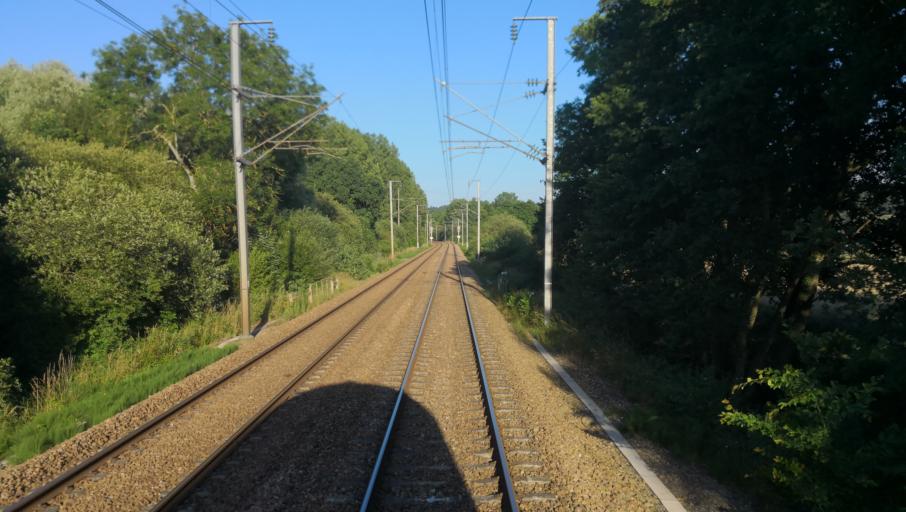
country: FR
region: Haute-Normandie
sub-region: Departement de l'Eure
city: Menneval
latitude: 49.0917
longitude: 0.6462
